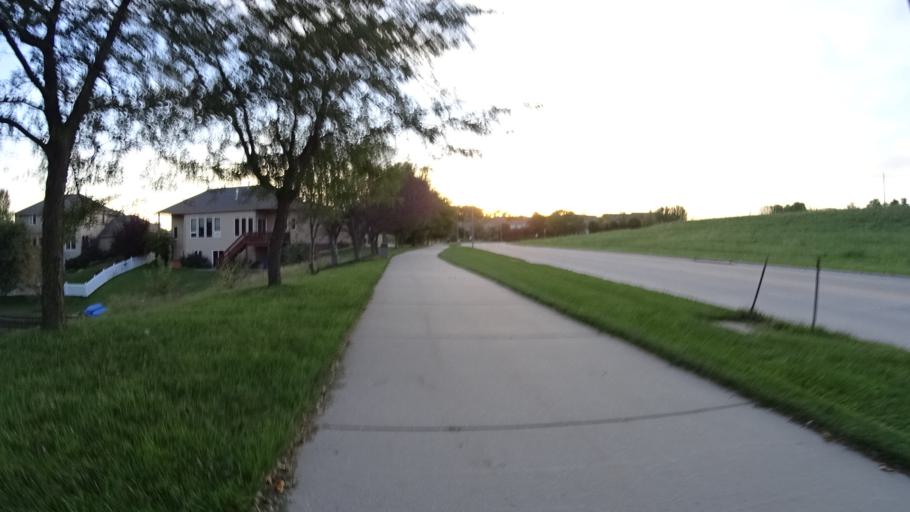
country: US
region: Nebraska
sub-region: Sarpy County
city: Papillion
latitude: 41.1382
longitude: -95.9835
